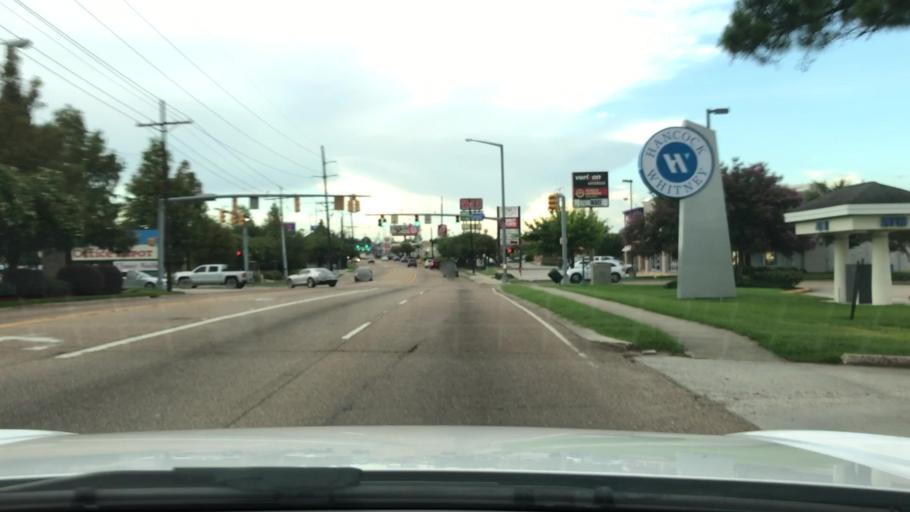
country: US
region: Louisiana
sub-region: East Baton Rouge Parish
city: Baton Rouge
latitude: 30.4180
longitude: -91.1422
